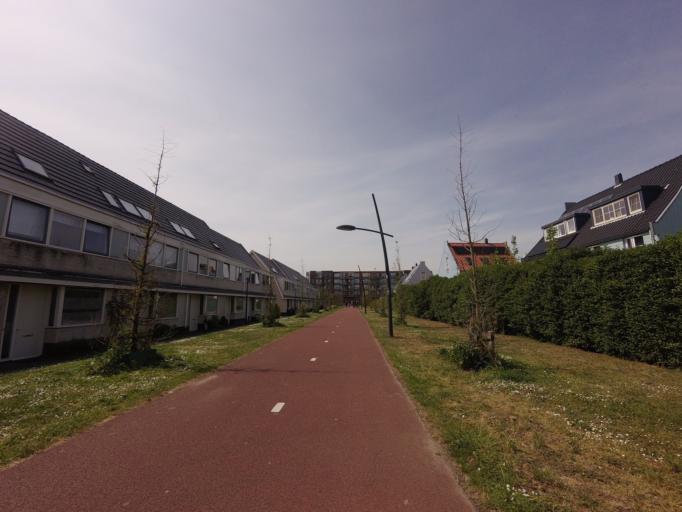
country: NL
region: North Holland
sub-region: Gemeente Uitgeest
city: Uitgeest
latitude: 52.4871
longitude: 4.7543
